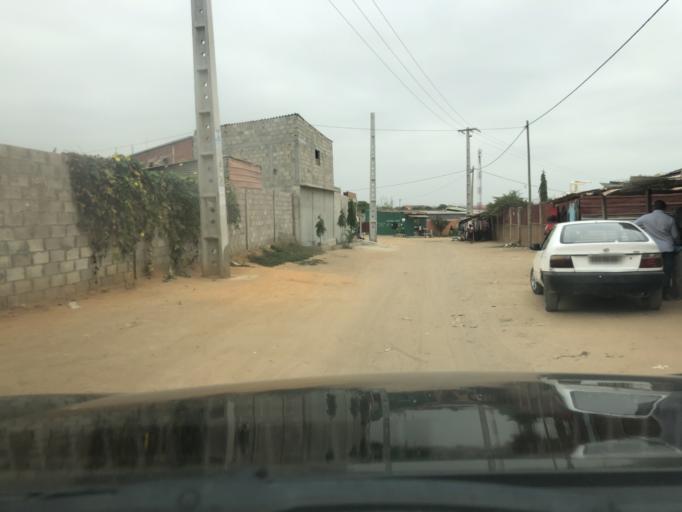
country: AO
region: Luanda
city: Luanda
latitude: -8.9367
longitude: 13.2256
